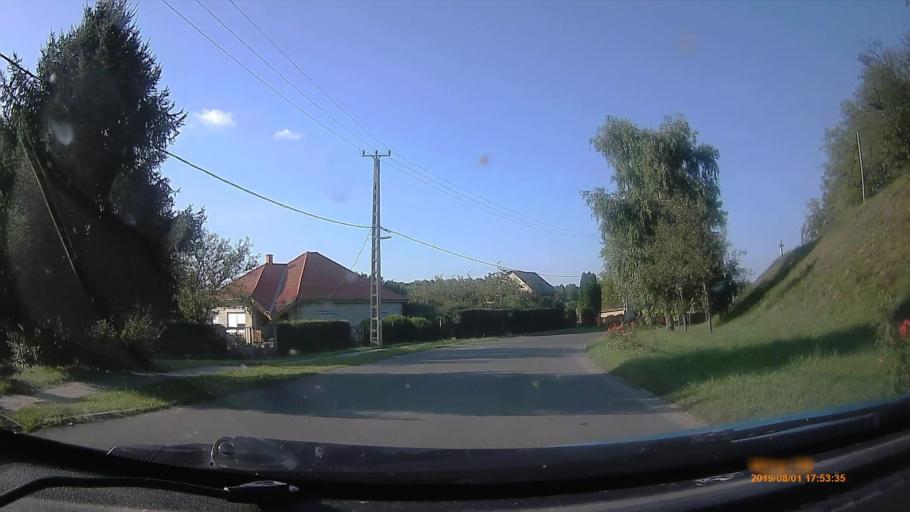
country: HU
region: Baranya
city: Sasd
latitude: 46.1902
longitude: 18.1531
